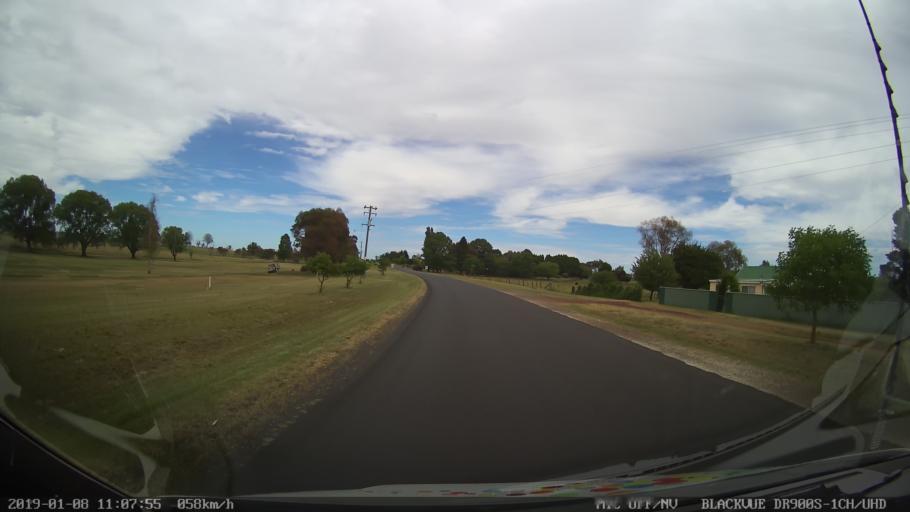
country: AU
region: New South Wales
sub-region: Guyra
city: Guyra
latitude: -30.2181
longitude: 151.6615
